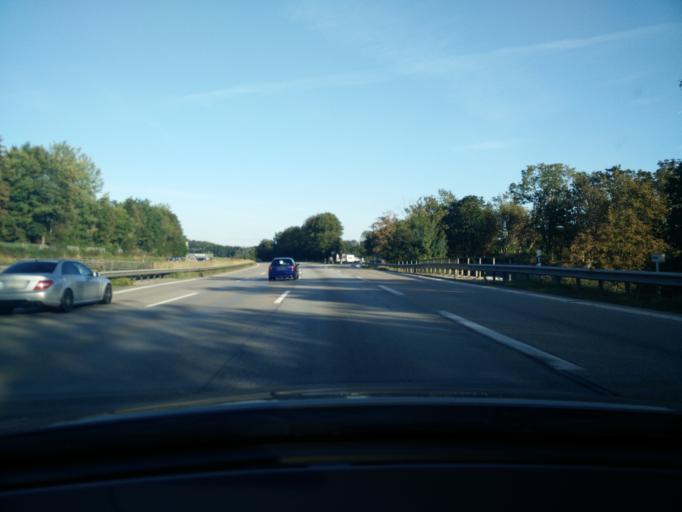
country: DE
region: Bavaria
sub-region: Upper Bavaria
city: Vagen
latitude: 47.8556
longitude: 11.8593
